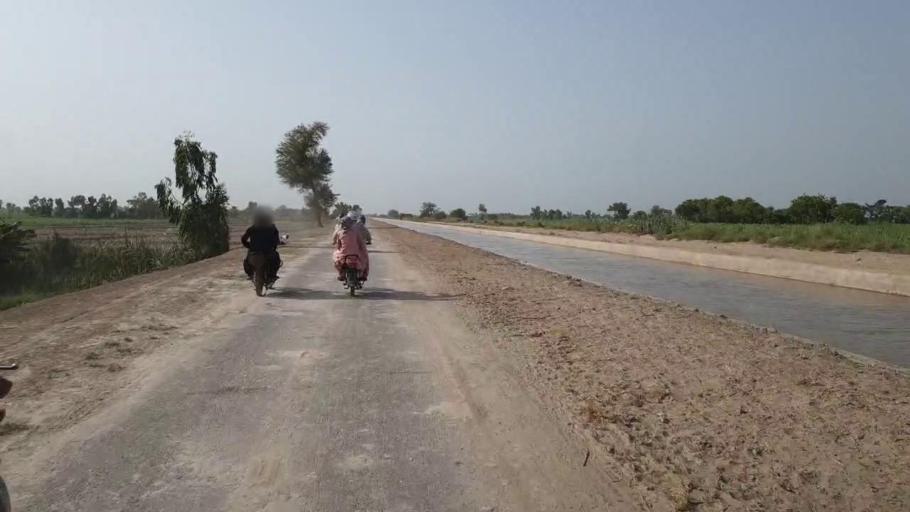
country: PK
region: Sindh
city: Daur
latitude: 26.3374
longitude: 68.1636
